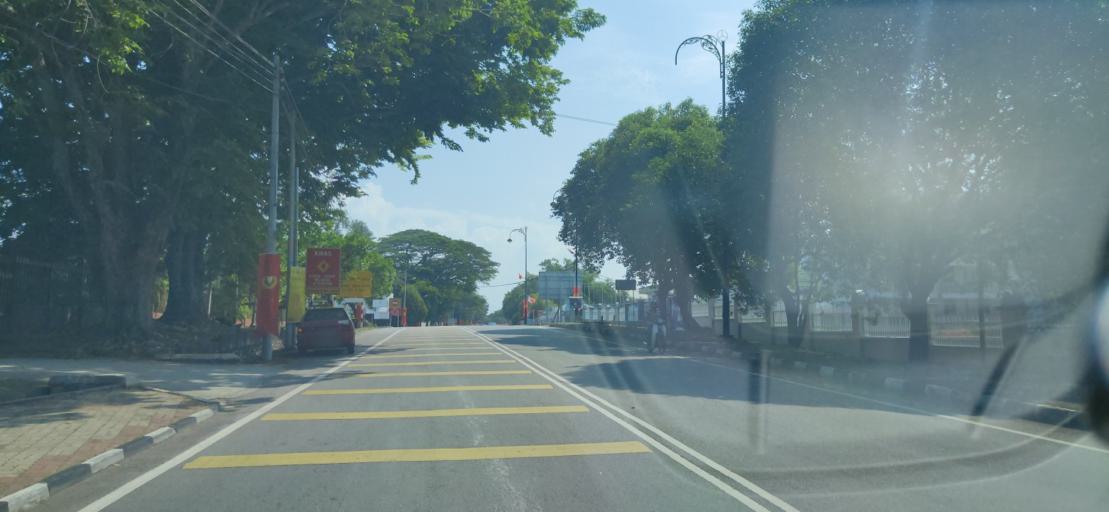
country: MY
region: Kedah
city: Sungai Petani
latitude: 5.6474
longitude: 100.4885
